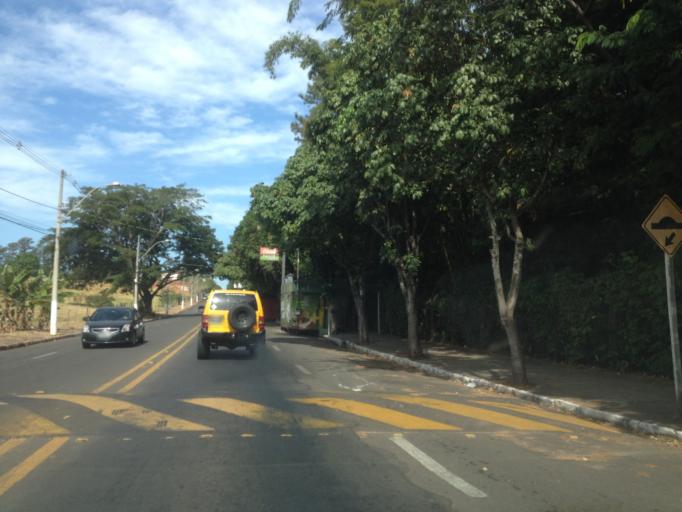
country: BR
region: Sao Paulo
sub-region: Marilia
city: Marilia
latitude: -22.2024
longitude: -49.9319
